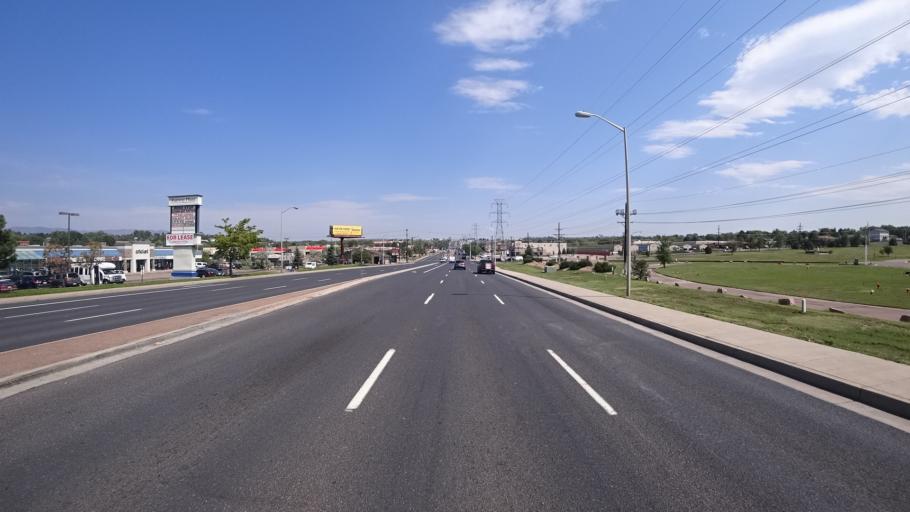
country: US
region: Colorado
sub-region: El Paso County
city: Stratmoor
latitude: 38.8238
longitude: -104.7574
